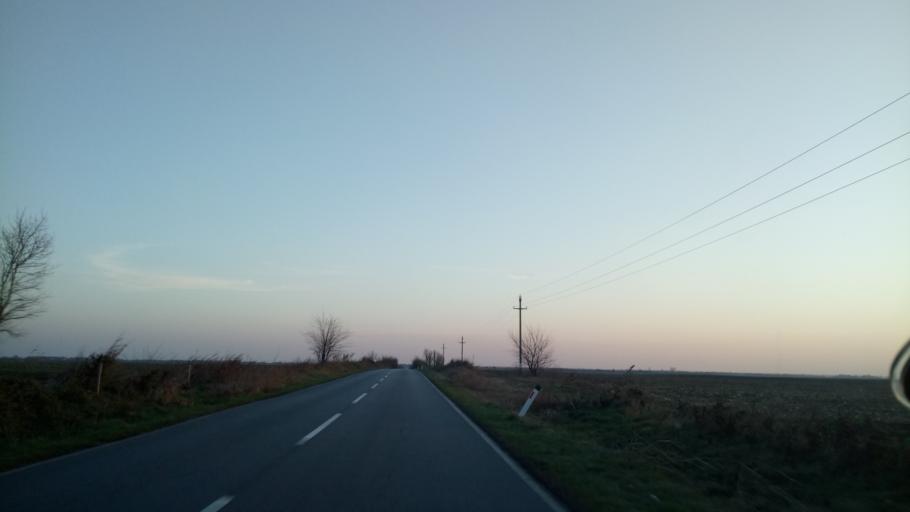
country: RS
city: Surduk
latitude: 45.0511
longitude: 20.3319
